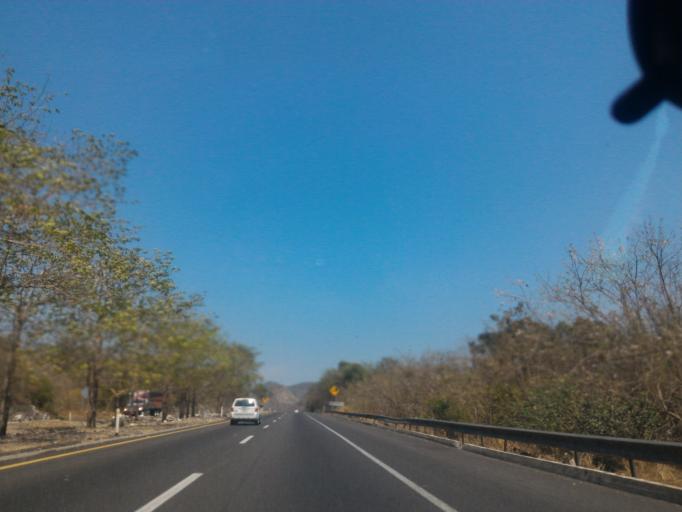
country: MX
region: Colima
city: Ixtlahuacan
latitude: 19.0347
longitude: -103.7926
